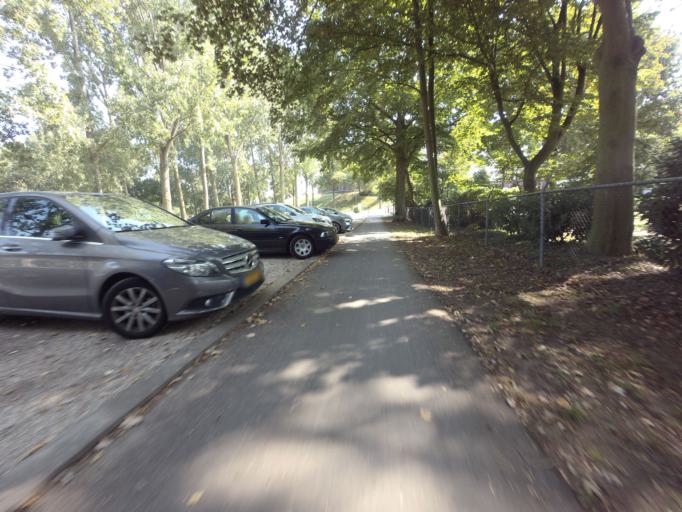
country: NL
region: Limburg
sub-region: Gemeente Roerdalen
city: Montfort
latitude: 51.1585
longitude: 5.9350
